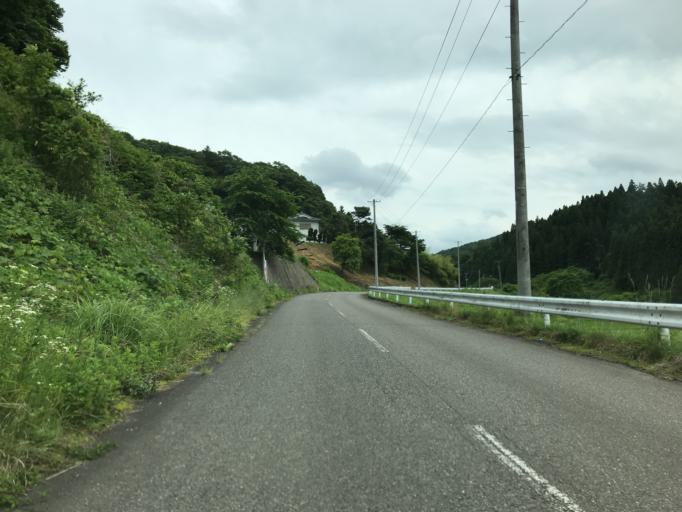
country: JP
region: Fukushima
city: Funehikimachi-funehiki
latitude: 37.4054
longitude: 140.6586
